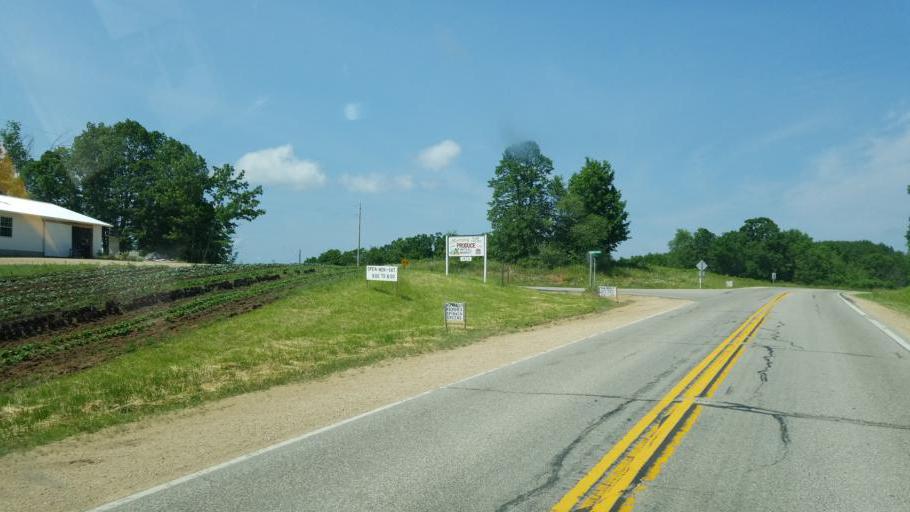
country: US
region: Wisconsin
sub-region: Vernon County
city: Hillsboro
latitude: 43.5956
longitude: -90.5063
